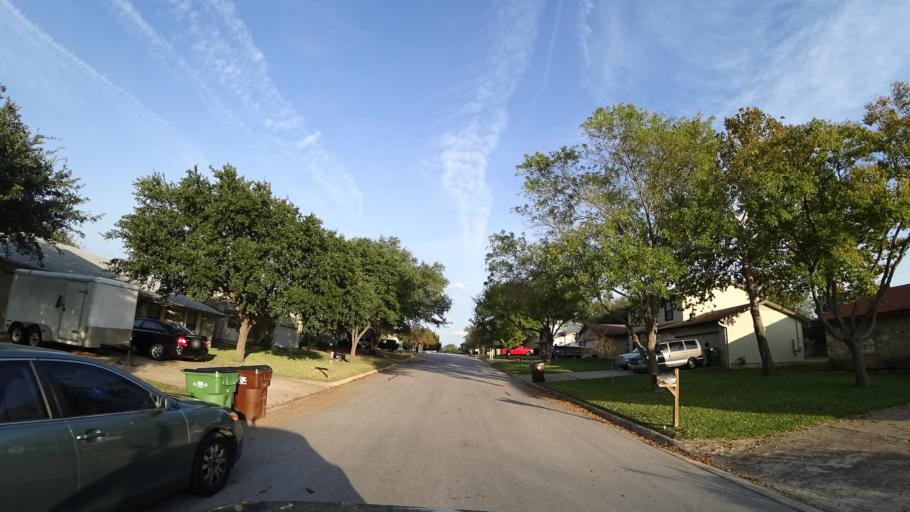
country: US
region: Texas
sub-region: Williamson County
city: Round Rock
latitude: 30.5032
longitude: -97.6685
